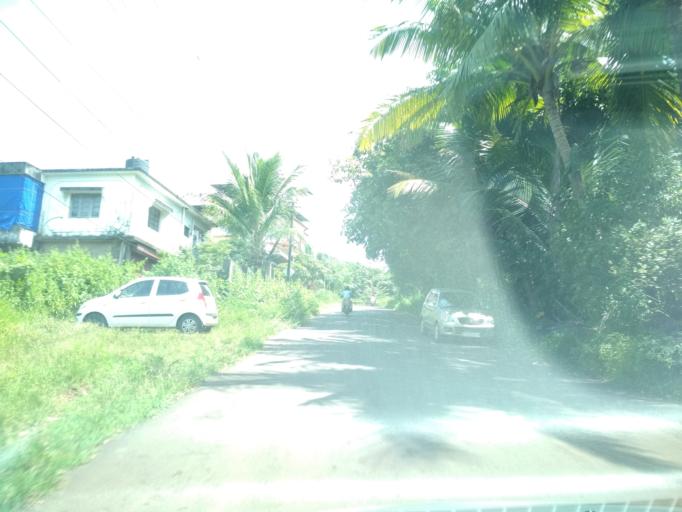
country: IN
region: Goa
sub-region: North Goa
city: Serula
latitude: 15.5459
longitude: 73.8214
